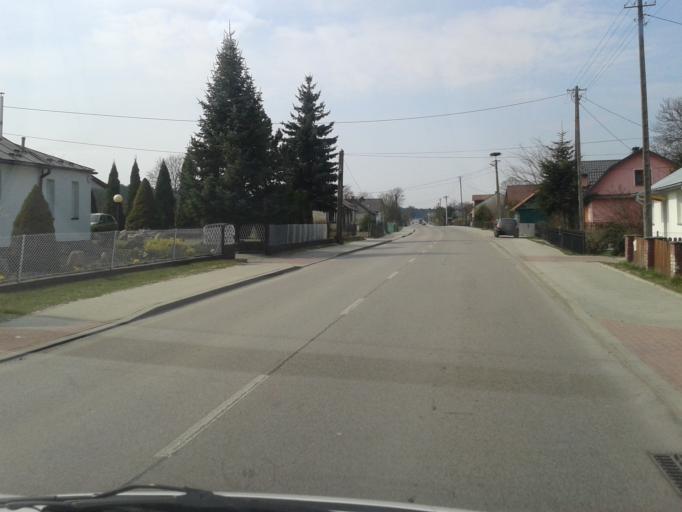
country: PL
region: Lublin Voivodeship
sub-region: Powiat tomaszowski
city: Belzec
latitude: 50.3821
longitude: 23.4108
